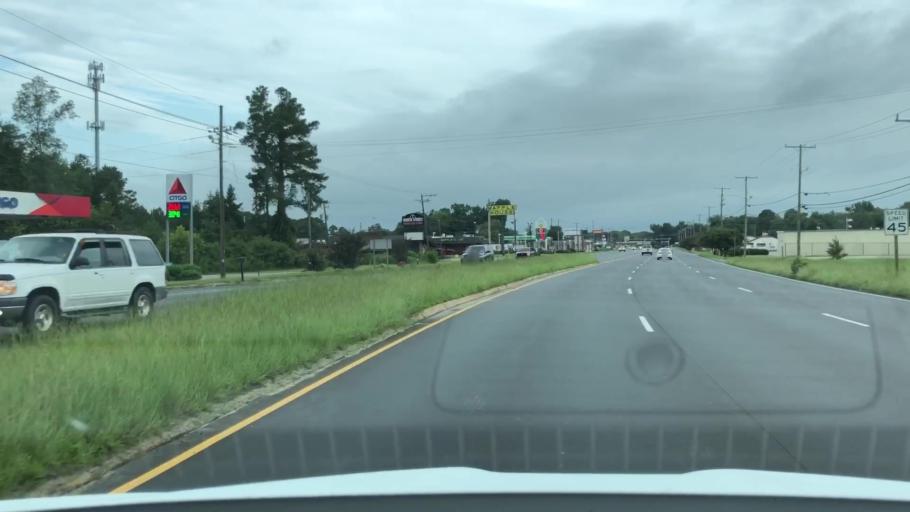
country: US
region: North Carolina
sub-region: Lenoir County
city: Kinston
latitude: 35.2378
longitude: -77.5744
